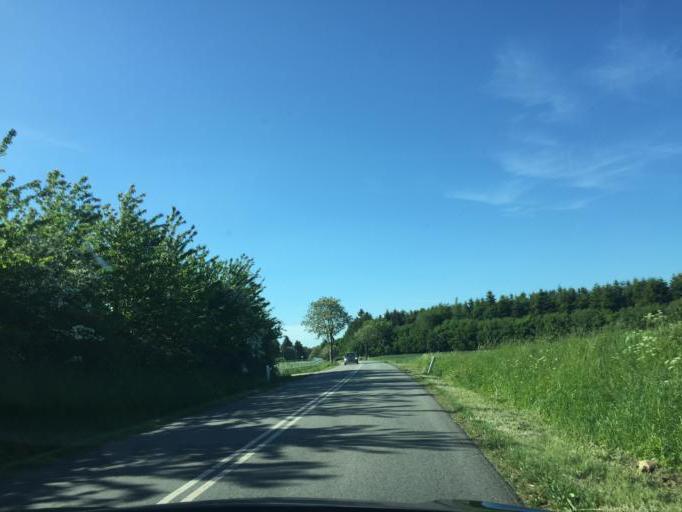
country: DK
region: Zealand
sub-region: Koge Kommune
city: Bjaeverskov
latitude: 55.4052
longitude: 12.0570
